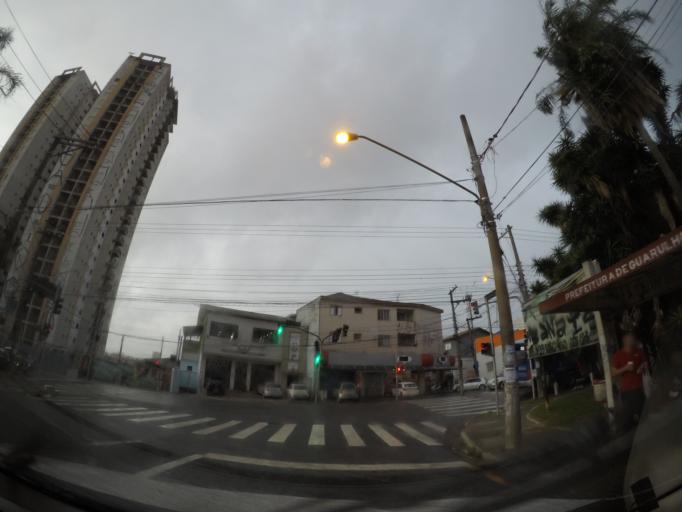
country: BR
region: Sao Paulo
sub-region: Guarulhos
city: Guarulhos
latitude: -23.4629
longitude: -46.5552
